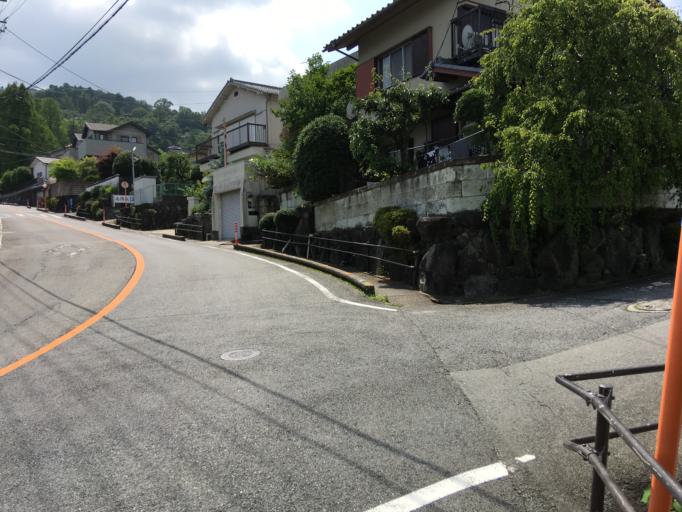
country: JP
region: Nara
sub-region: Ikoma-shi
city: Ikoma
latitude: 34.6903
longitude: 135.6919
